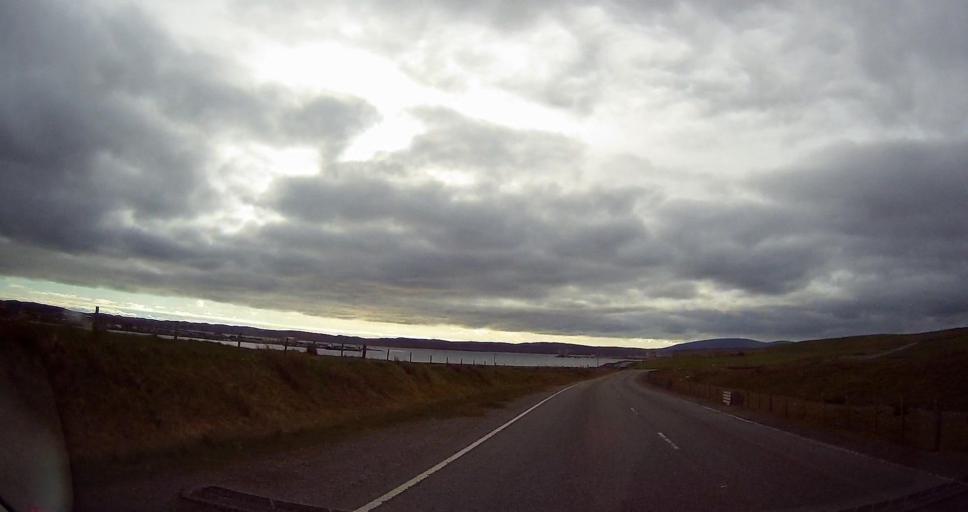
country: GB
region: Scotland
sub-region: Shetland Islands
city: Lerwick
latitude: 60.4456
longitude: -1.2485
